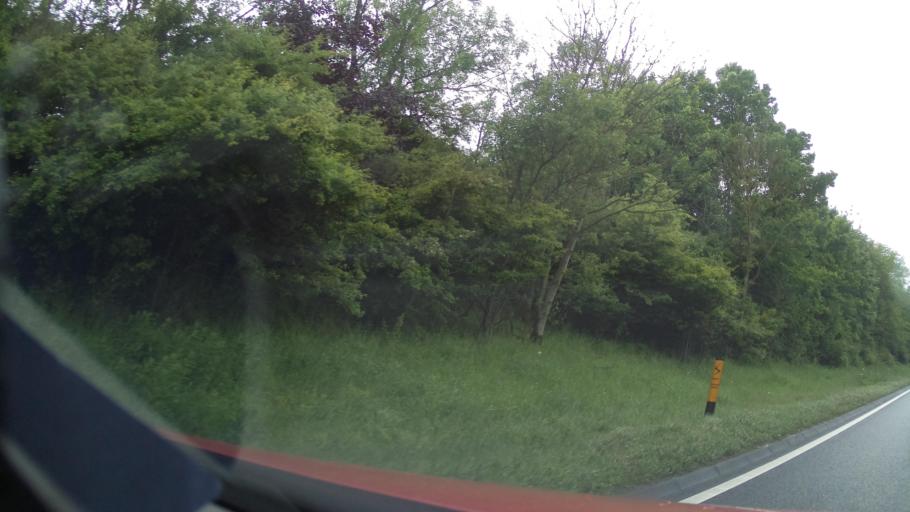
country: GB
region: England
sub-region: Sunderland
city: Ryhope
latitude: 54.8513
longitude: -1.3996
